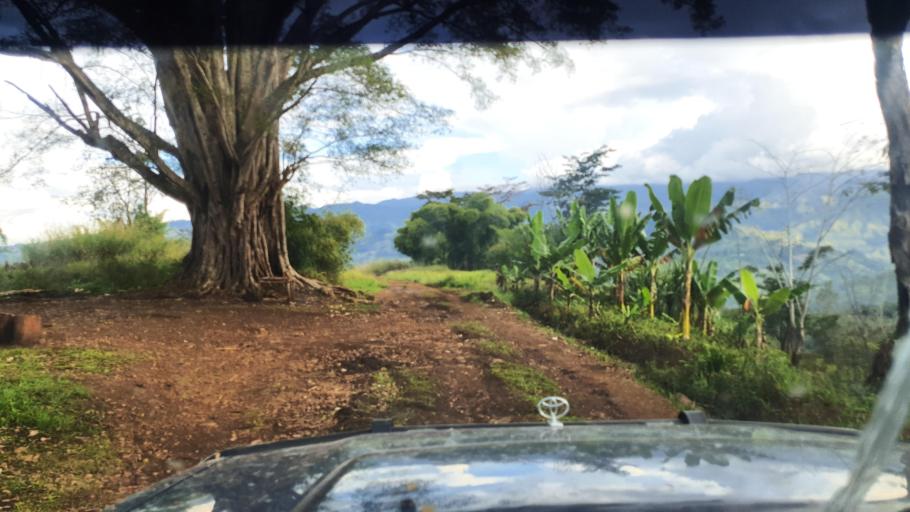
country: PG
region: Jiwaka
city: Minj
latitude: -5.9290
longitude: 144.8196
